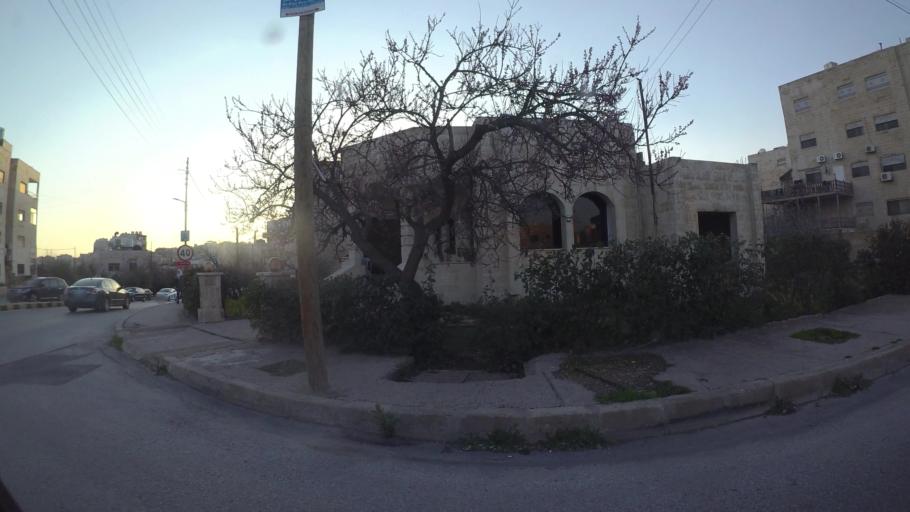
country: JO
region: Amman
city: Al Jubayhah
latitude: 31.9987
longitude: 35.8625
